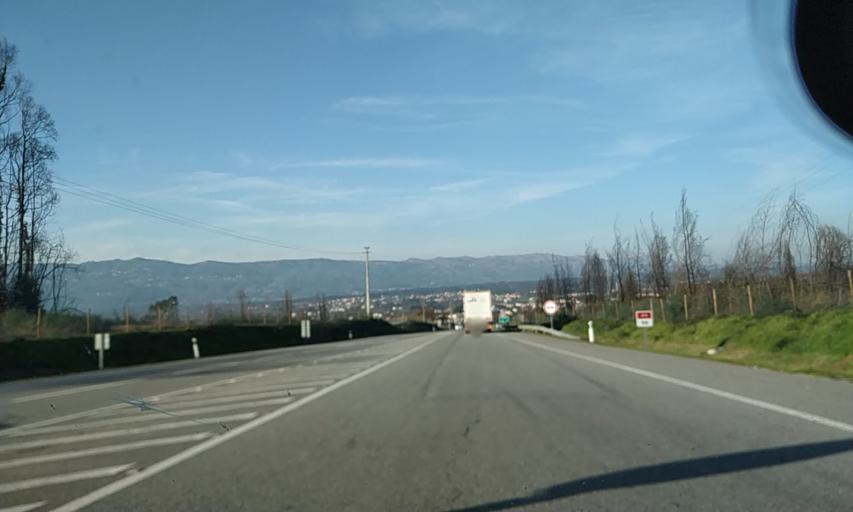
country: PT
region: Viseu
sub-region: Concelho de Tondela
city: Tondela
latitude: 40.5037
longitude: -8.0838
